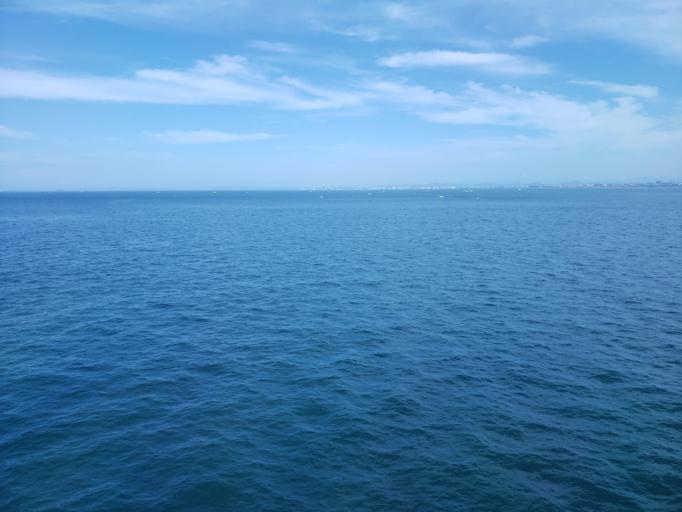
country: JP
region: Hyogo
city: Akashi
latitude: 34.6121
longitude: 134.9334
